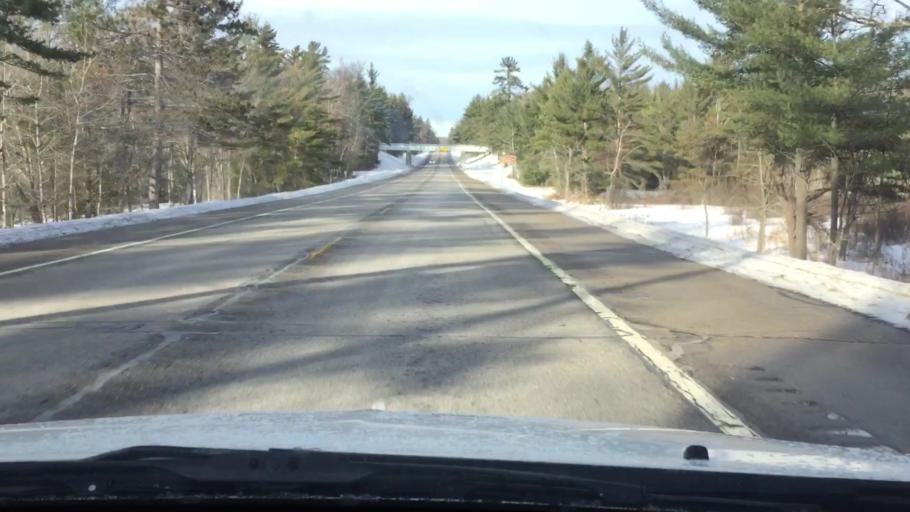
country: US
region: Michigan
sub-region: Wexford County
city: Manton
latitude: 44.5618
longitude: -85.3672
